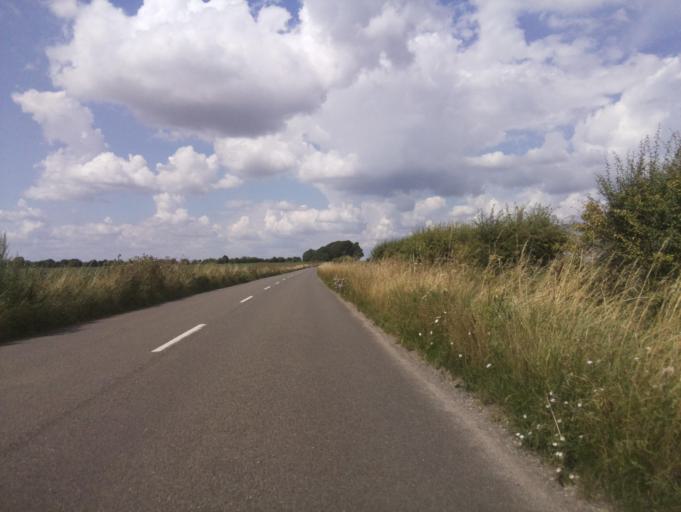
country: GB
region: England
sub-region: Borough of Swindon
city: Bishopstone
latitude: 51.5537
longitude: -1.6033
